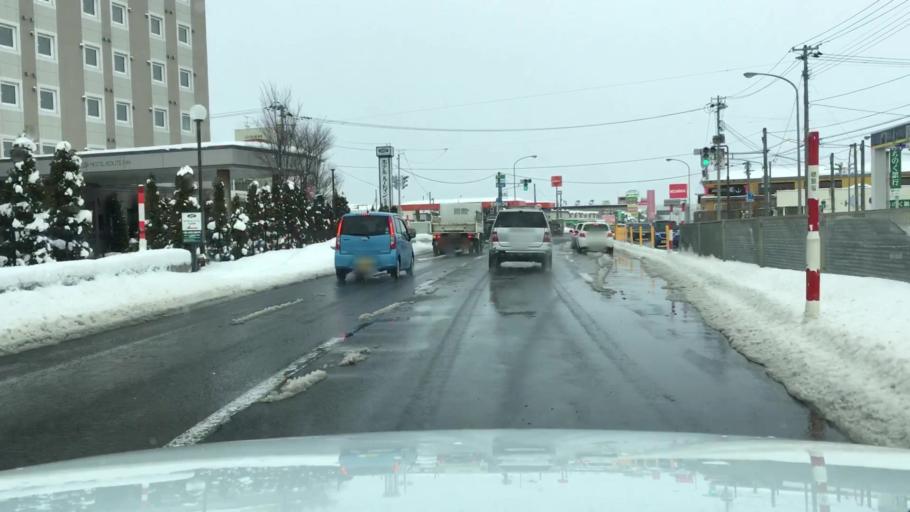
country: JP
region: Aomori
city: Hirosaki
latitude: 40.6030
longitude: 140.4994
